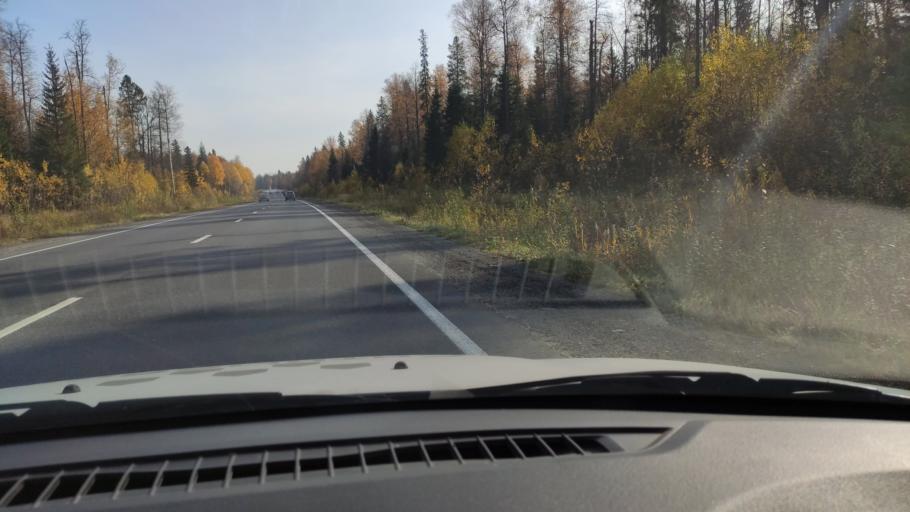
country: RU
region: Perm
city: Novyye Lyady
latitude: 58.0292
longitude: 56.4940
